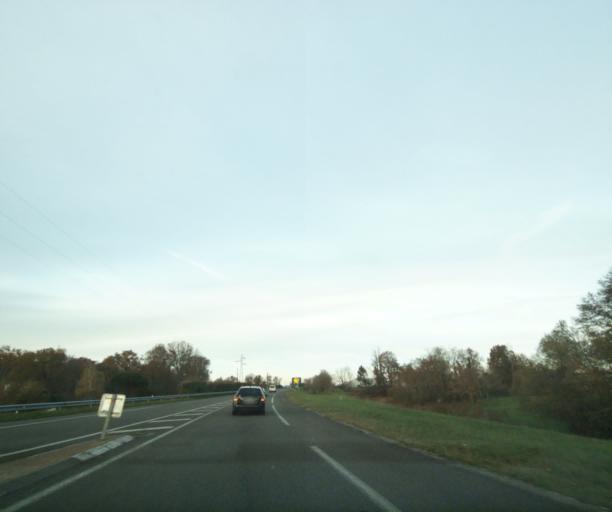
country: FR
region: Aquitaine
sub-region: Departement de la Gironde
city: Bazas
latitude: 44.4375
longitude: -0.2389
